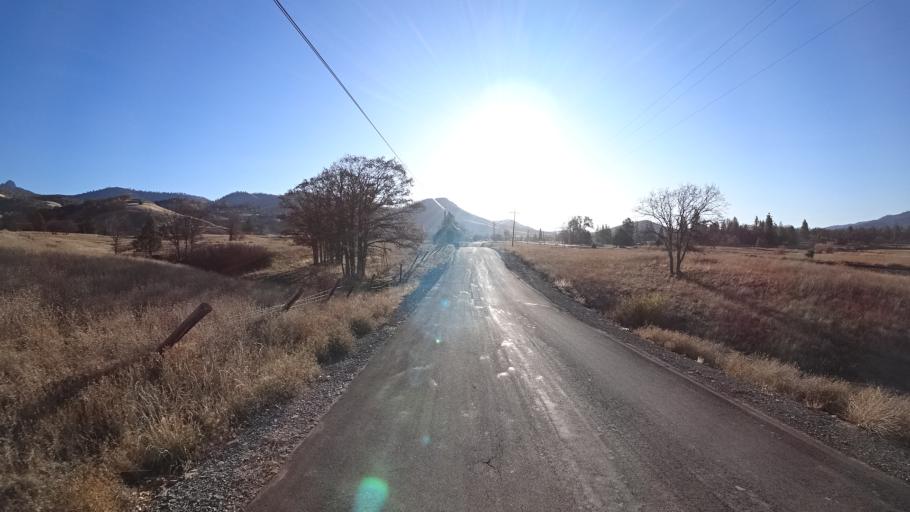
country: US
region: Oregon
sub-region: Jackson County
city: Ashland
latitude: 41.9976
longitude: -122.6293
